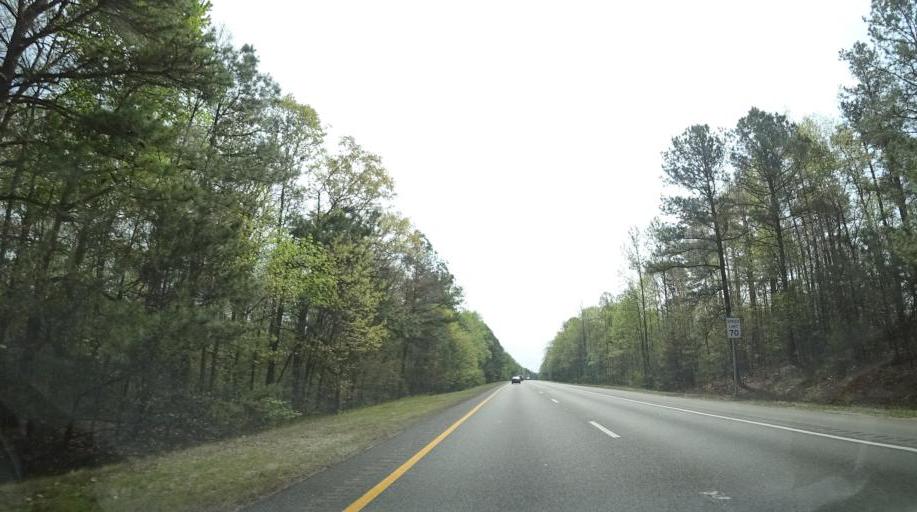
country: US
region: Virginia
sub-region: King William County
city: West Point
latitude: 37.4166
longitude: -76.8091
